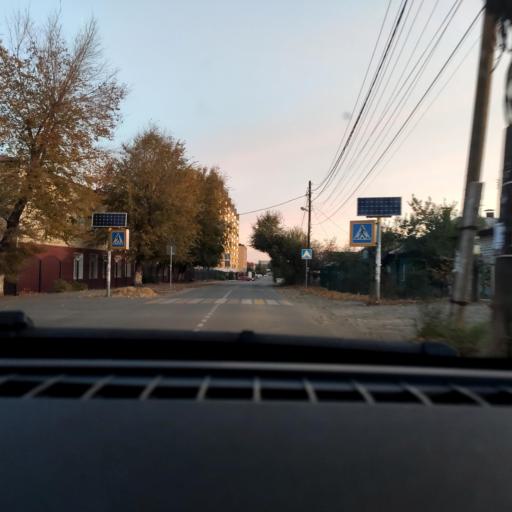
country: RU
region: Voronezj
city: Voronezh
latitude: 51.6636
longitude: 39.2802
